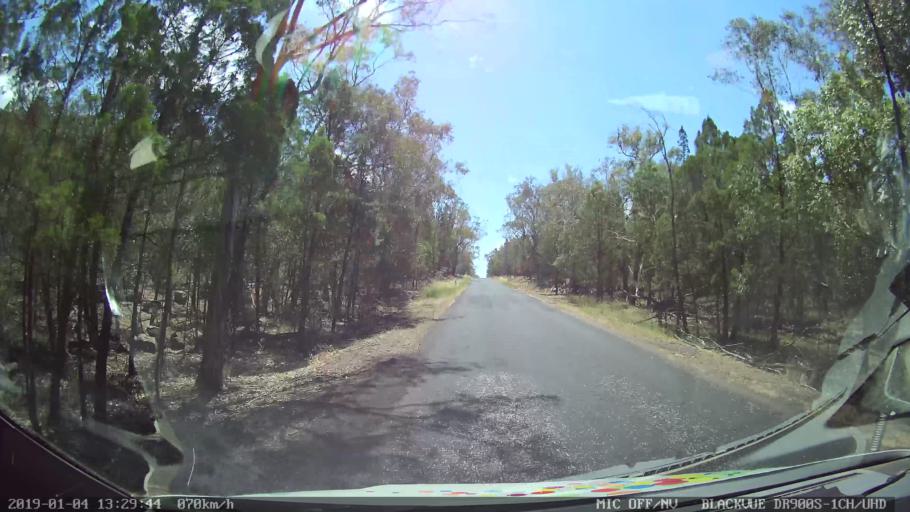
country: AU
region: New South Wales
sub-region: Parkes
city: Peak Hill
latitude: -32.6432
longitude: 148.5505
